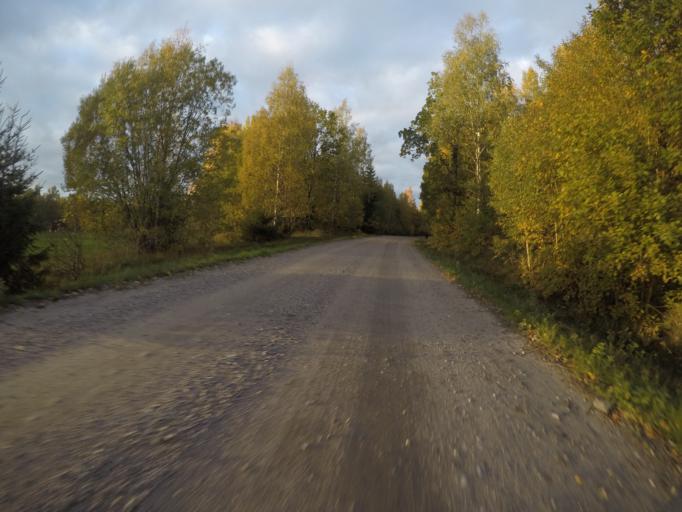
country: SE
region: Vaestmanland
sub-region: Arboga Kommun
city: Tyringe
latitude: 59.3162
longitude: 15.9796
